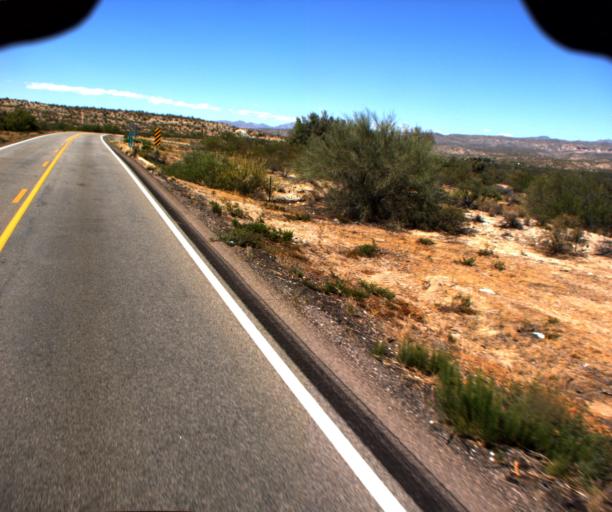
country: US
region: Arizona
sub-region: Yavapai County
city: Bagdad
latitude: 34.7860
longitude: -113.6237
